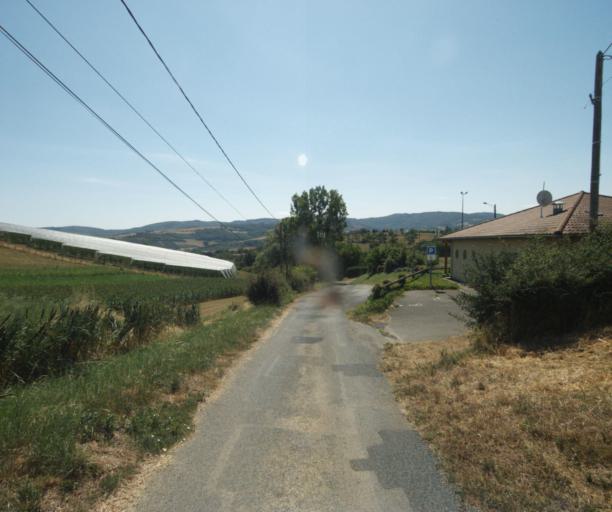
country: FR
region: Rhone-Alpes
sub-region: Departement du Rhone
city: Bessenay
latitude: 45.7916
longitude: 4.5590
